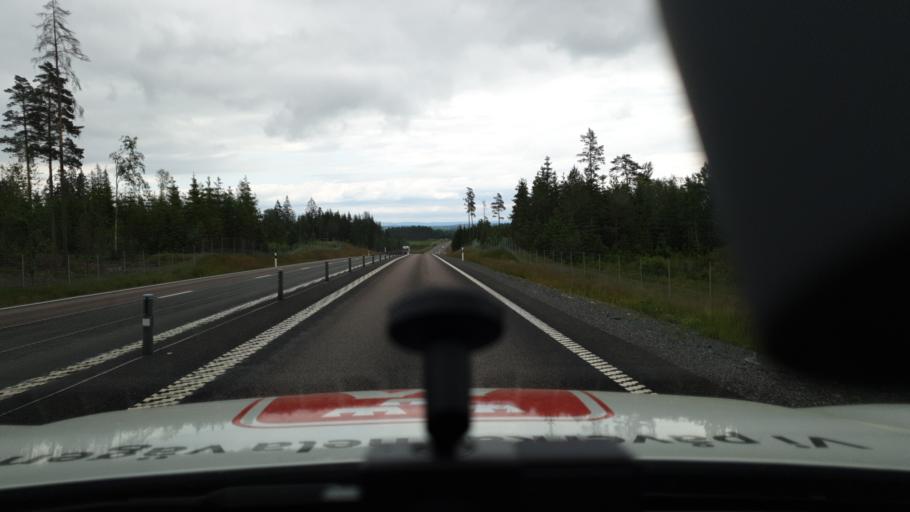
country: SE
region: Joenkoeping
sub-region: Mullsjo Kommun
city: Mullsjoe
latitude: 57.8736
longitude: 13.9358
